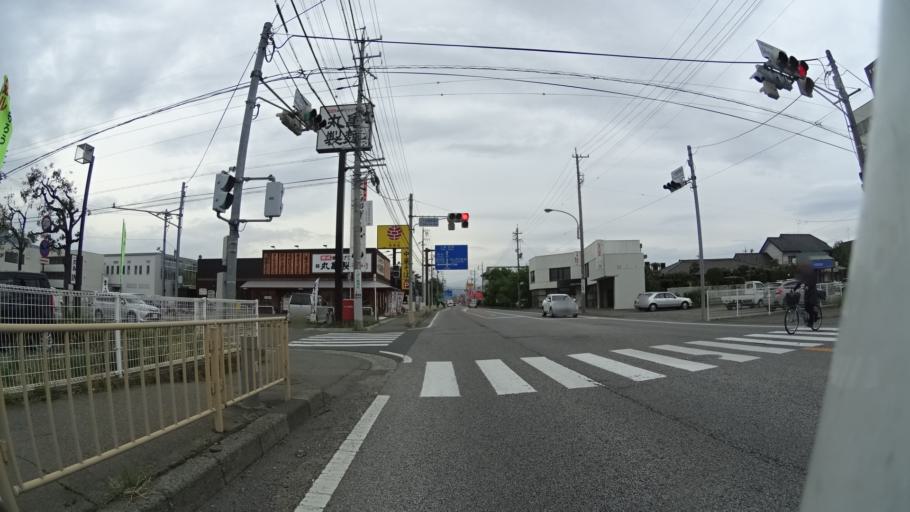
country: JP
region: Nagano
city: Nagano-shi
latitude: 36.5353
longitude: 138.1228
